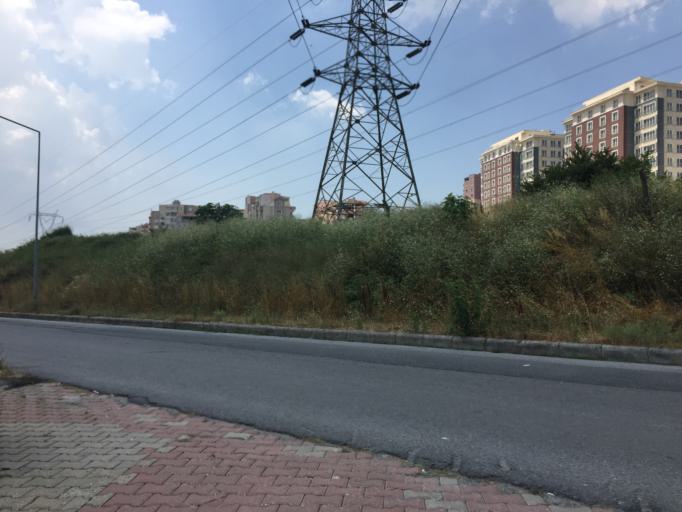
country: TR
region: Istanbul
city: Esenyurt
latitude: 41.0782
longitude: 28.6709
